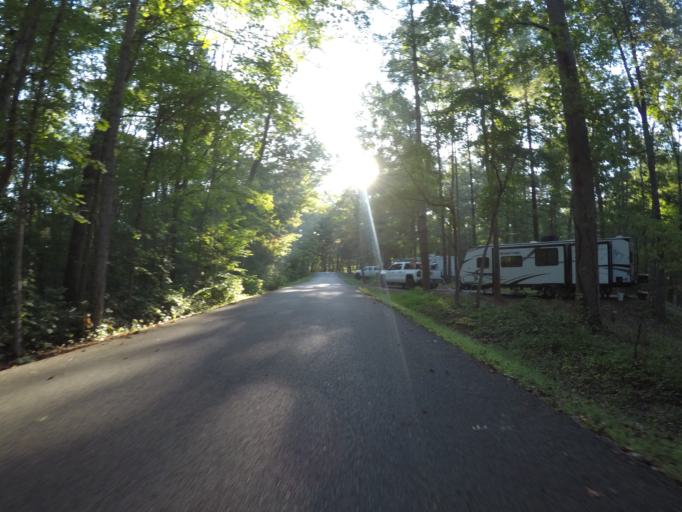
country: US
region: Ohio
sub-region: Lawrence County
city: Ironton
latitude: 38.6116
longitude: -82.6190
